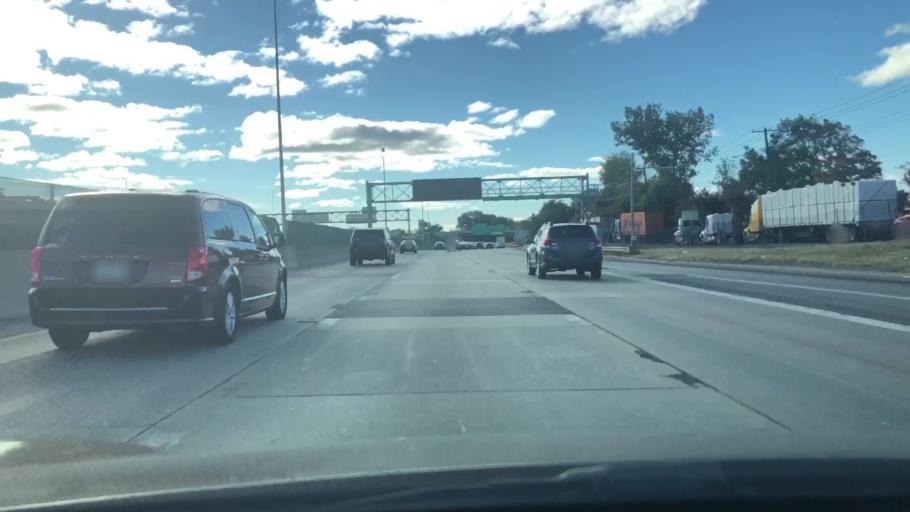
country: US
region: New York
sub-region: Bronx
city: Eastchester
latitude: 40.8654
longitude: -73.8312
